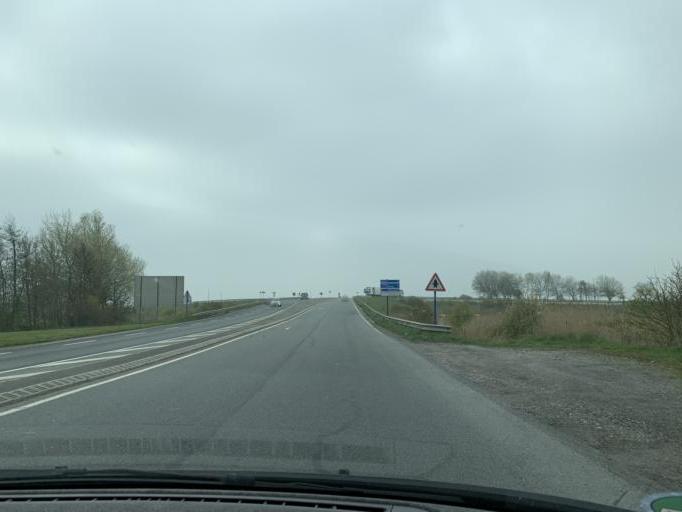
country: FR
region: Nord-Pas-de-Calais
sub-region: Departement du Pas-de-Calais
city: Marck
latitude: 50.9404
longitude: 1.9404
